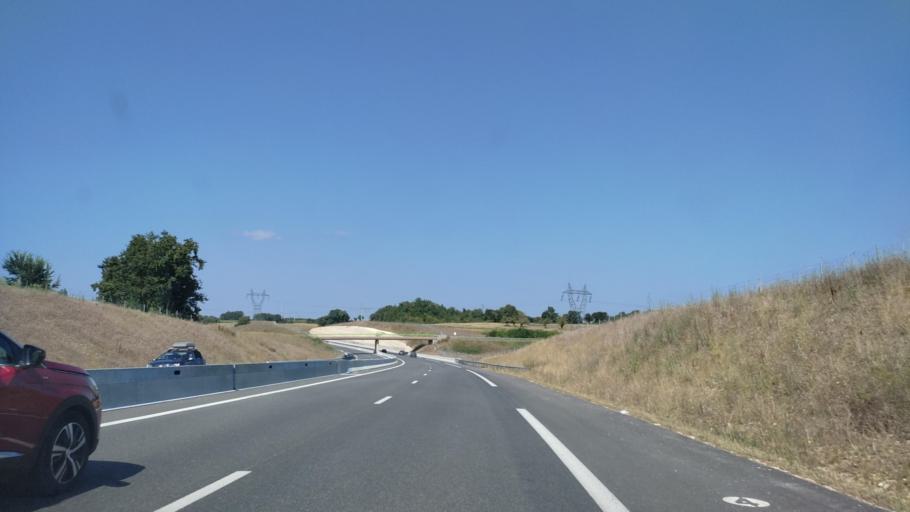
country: FR
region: Poitou-Charentes
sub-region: Departement de la Charente
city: Fleac
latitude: 45.6851
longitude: 0.0795
